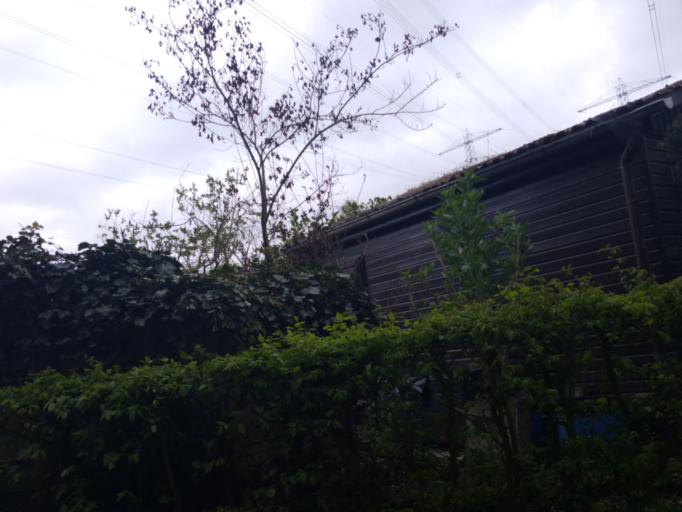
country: DE
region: Schleswig-Holstein
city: Oststeinbek
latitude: 53.5158
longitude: 10.1774
